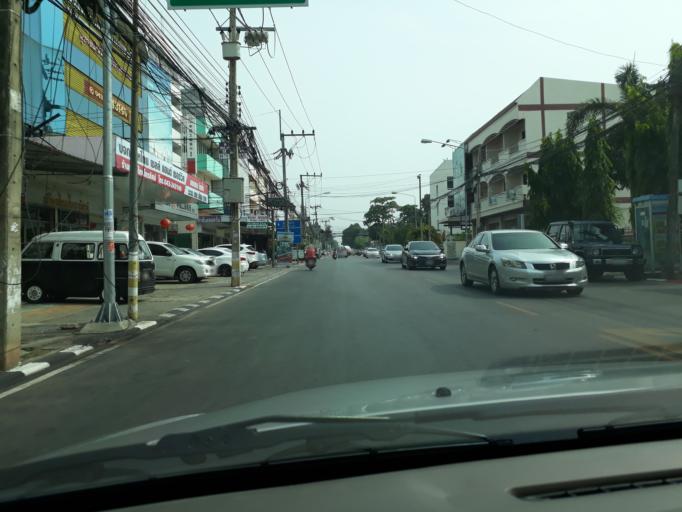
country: TH
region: Khon Kaen
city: Khon Kaen
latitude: 16.4372
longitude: 102.8364
